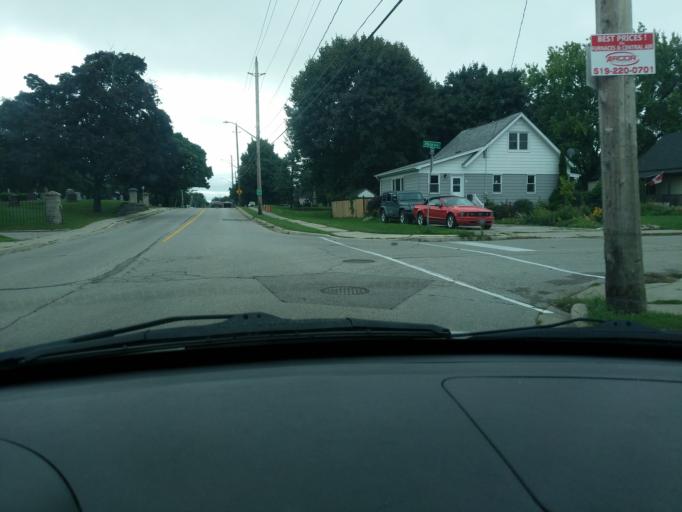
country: CA
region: Ontario
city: Cambridge
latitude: 43.4287
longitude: -80.2990
